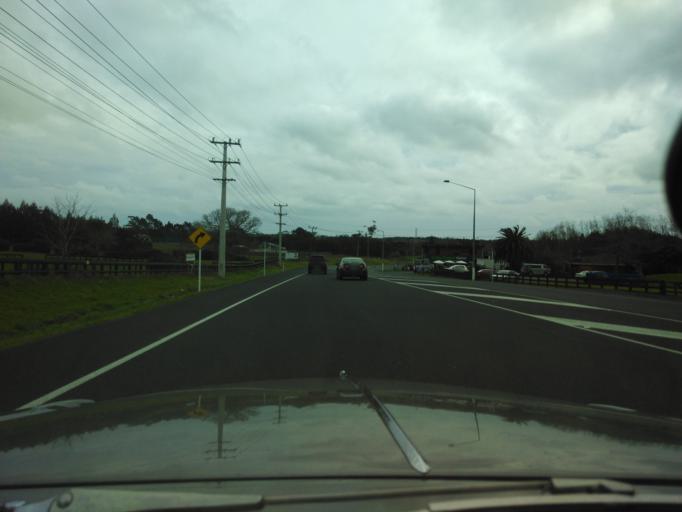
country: NZ
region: Auckland
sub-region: Auckland
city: Rosebank
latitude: -36.7873
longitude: 174.5756
